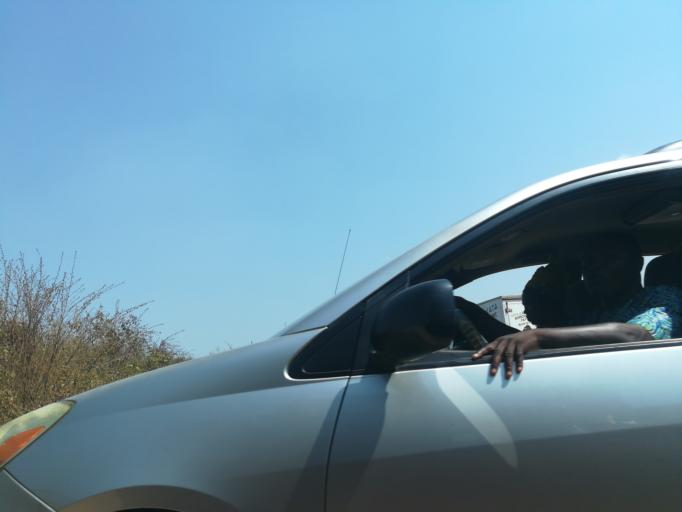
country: NG
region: Abuja Federal Capital Territory
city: Abuja
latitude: 9.0594
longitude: 7.4214
